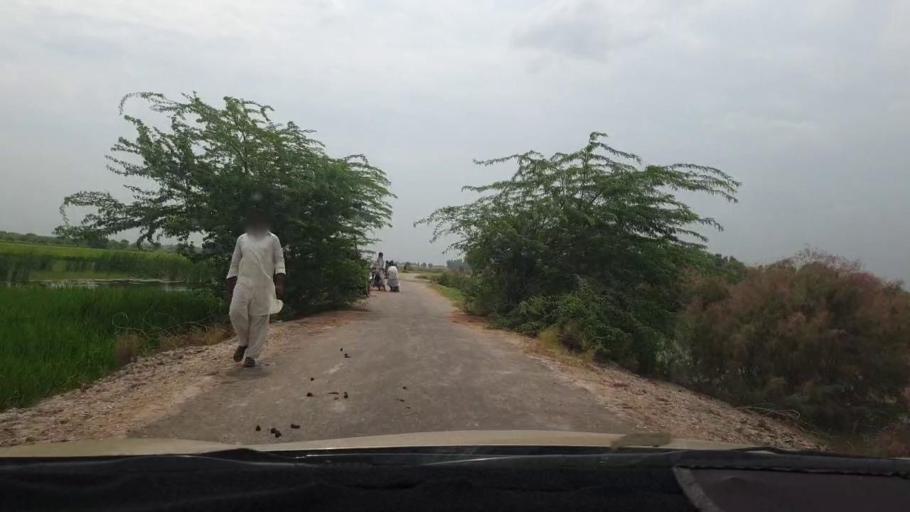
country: PK
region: Sindh
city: Naudero
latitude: 27.6274
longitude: 68.3196
